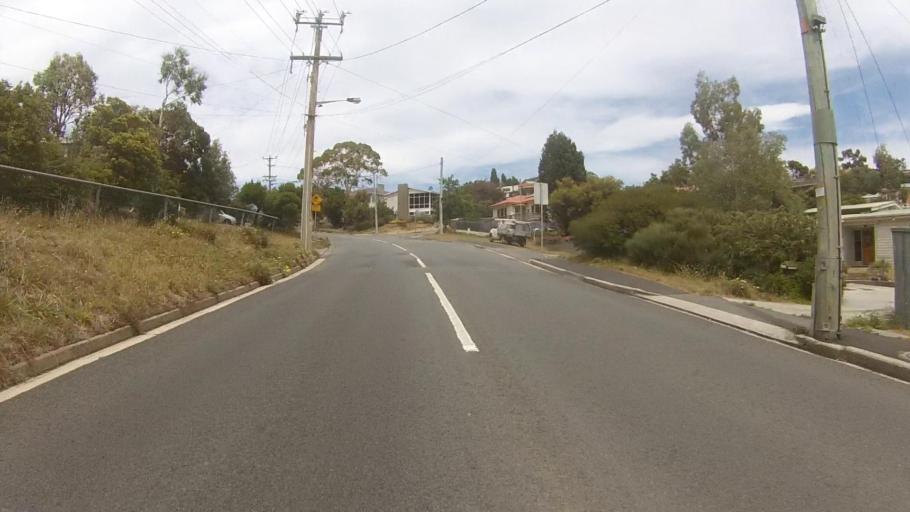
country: AU
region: Tasmania
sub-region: Clarence
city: Lindisfarne
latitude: -42.8544
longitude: 147.3712
